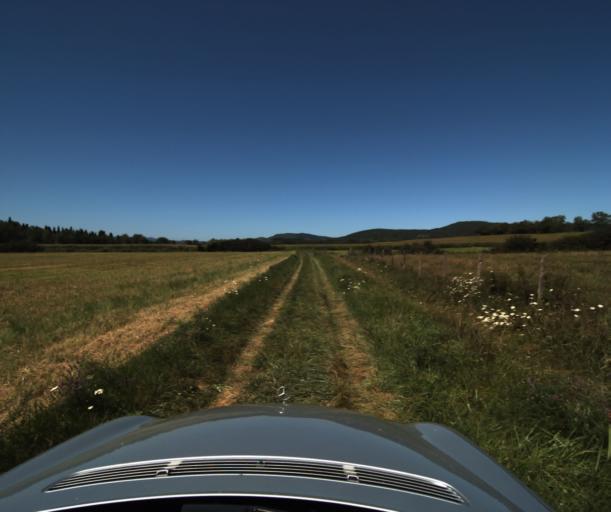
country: FR
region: Languedoc-Roussillon
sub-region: Departement de l'Aude
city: Chalabre
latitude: 42.9885
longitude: 1.9274
